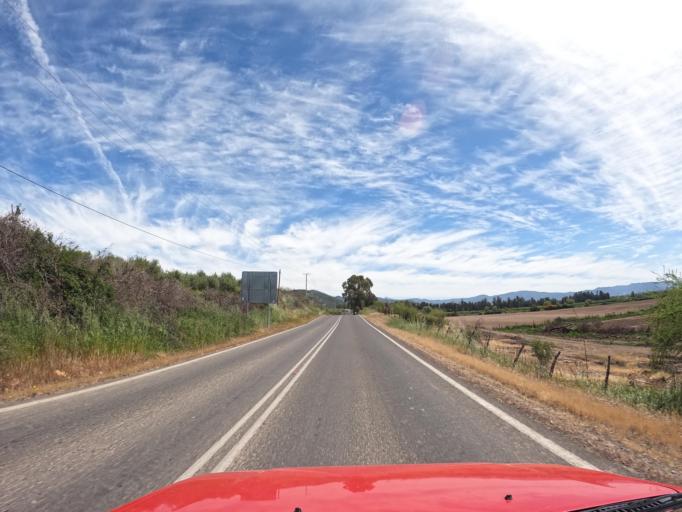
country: CL
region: Maule
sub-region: Provincia de Talca
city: Talca
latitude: -35.1136
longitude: -71.6357
